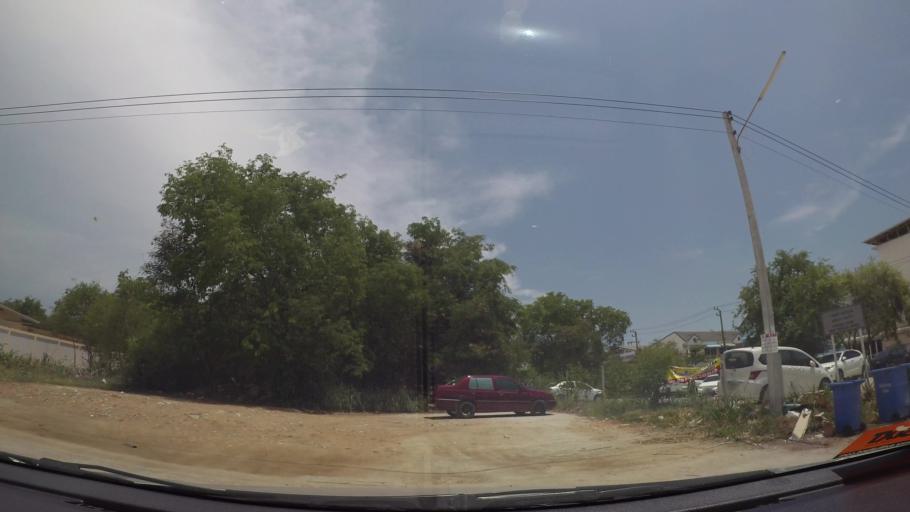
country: TH
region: Chon Buri
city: Chon Buri
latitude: 13.3398
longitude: 100.9412
